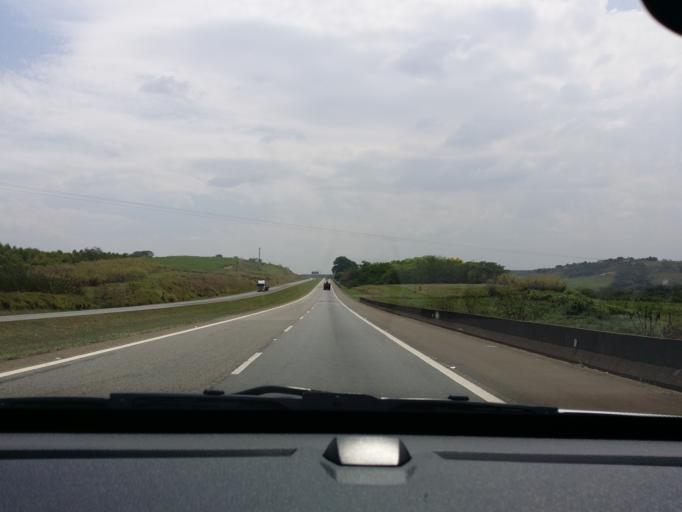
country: BR
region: Sao Paulo
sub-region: Santa Barbara D'Oeste
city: Santa Barbara d'Oeste
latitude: -22.6582
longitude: -47.4492
